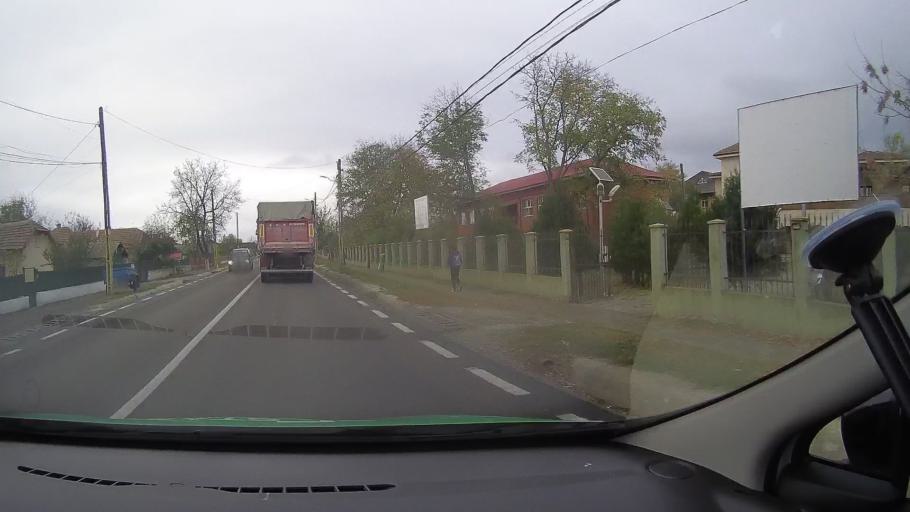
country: RO
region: Constanta
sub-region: Comuna Poarta Alba
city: Poarta Alba
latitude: 44.2088
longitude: 28.3947
